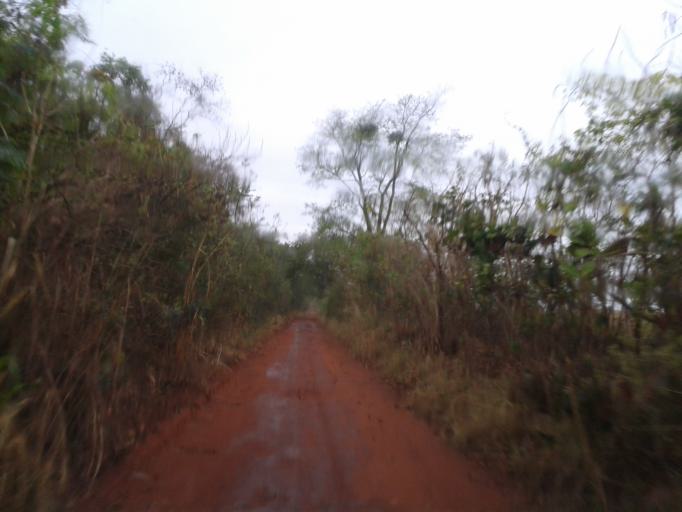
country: BR
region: Minas Gerais
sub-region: Campina Verde
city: Campina Verde
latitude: -19.3493
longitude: -49.5309
